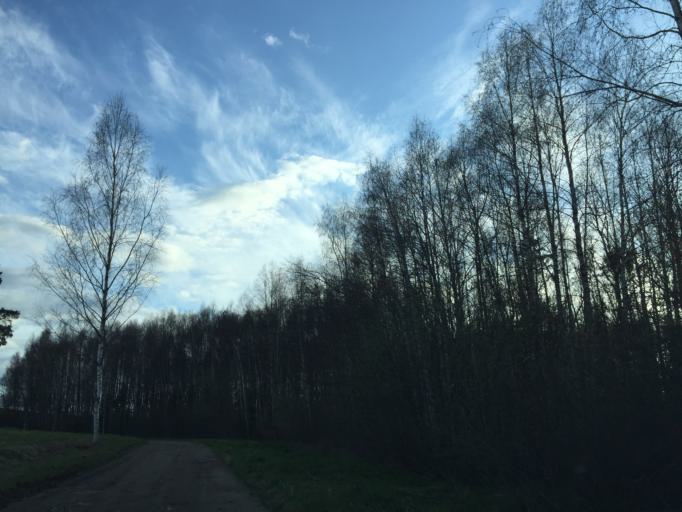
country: LV
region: Rezekne
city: Rezekne
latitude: 56.5832
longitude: 27.3433
